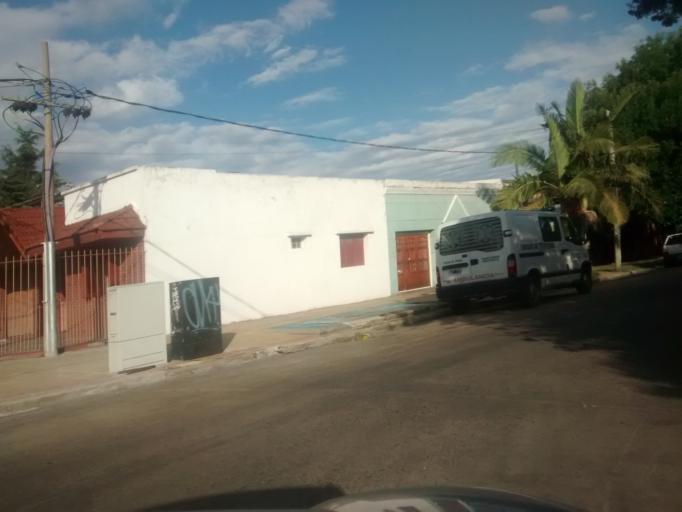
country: AR
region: Buenos Aires
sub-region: Partido de La Plata
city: La Plata
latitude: -34.9426
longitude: -57.9467
